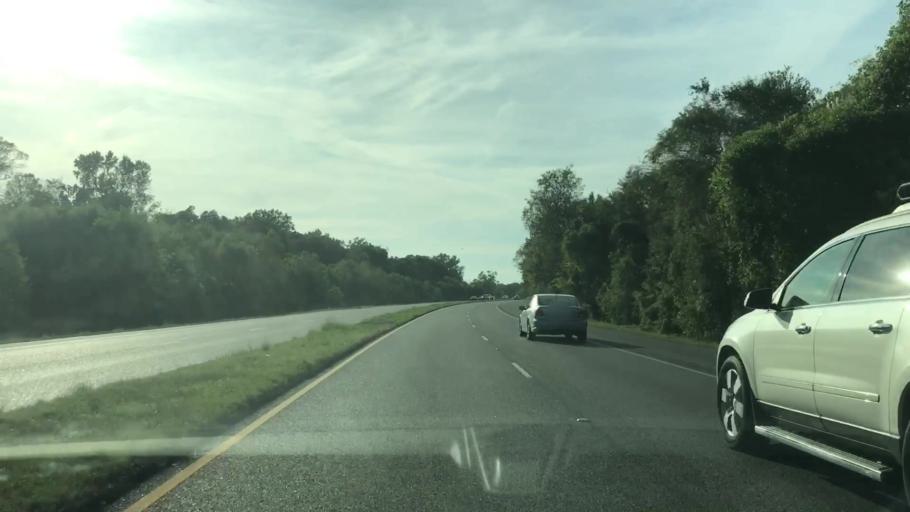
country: US
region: Louisiana
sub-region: Jefferson Parish
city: Avondale
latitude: 29.9096
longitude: -90.1845
